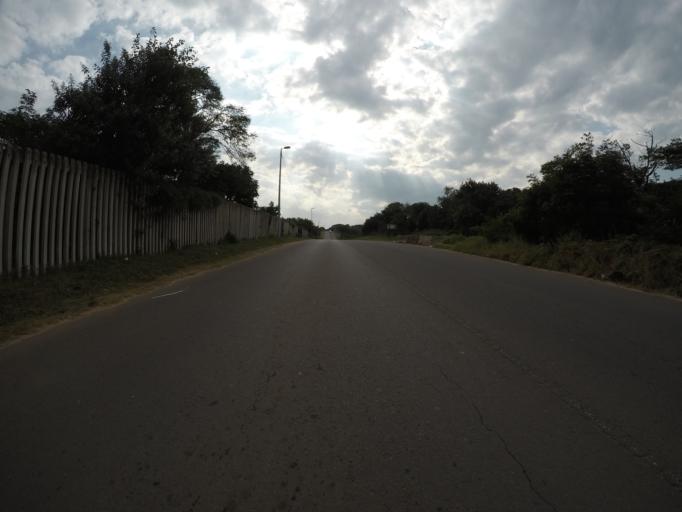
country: ZA
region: KwaZulu-Natal
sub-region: uThungulu District Municipality
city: Richards Bay
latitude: -28.7457
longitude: 32.0846
